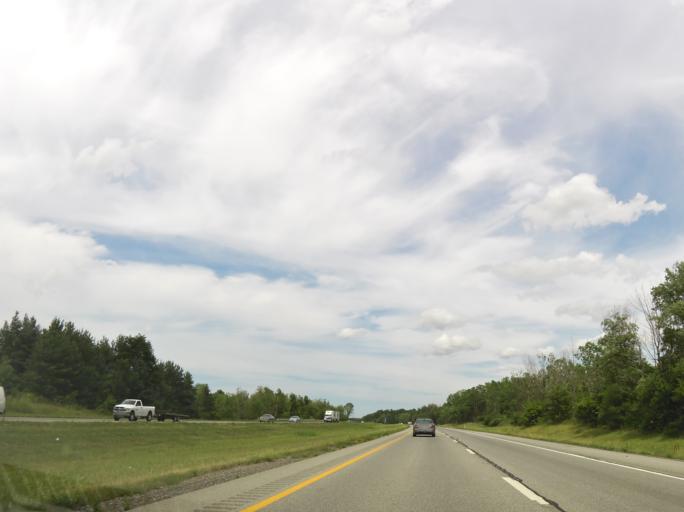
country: US
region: Ohio
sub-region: Lake County
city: Perry
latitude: 41.7230
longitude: -81.1237
